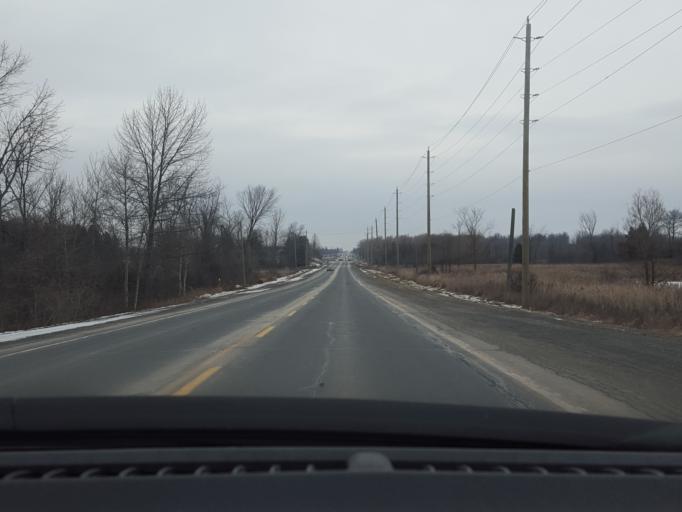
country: CA
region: Ontario
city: Keswick
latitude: 44.1836
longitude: -79.4359
